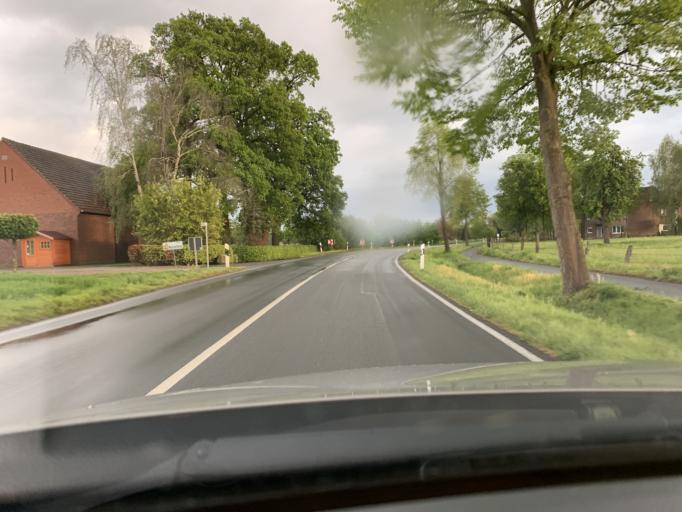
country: DE
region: North Rhine-Westphalia
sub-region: Regierungsbezirk Detmold
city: Langenberg
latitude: 51.7919
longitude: 8.3714
